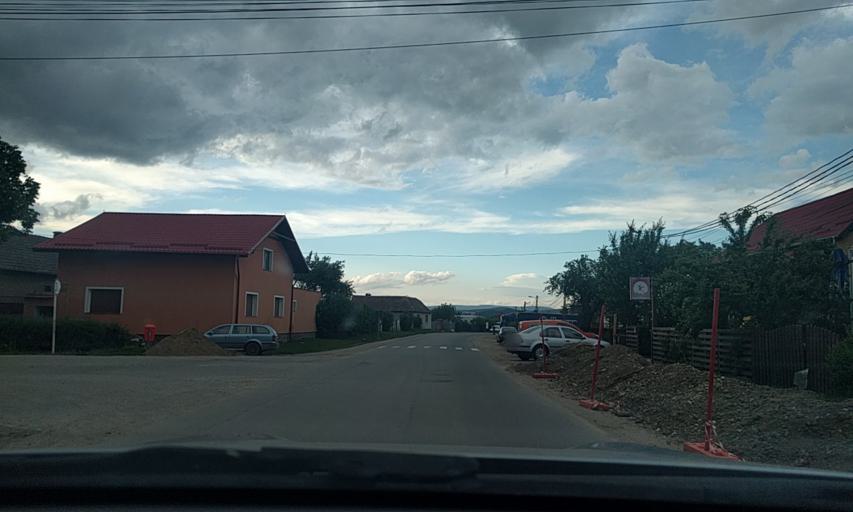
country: RO
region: Brasov
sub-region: Comuna Harman
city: Harman
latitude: 45.7171
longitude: 25.6944
